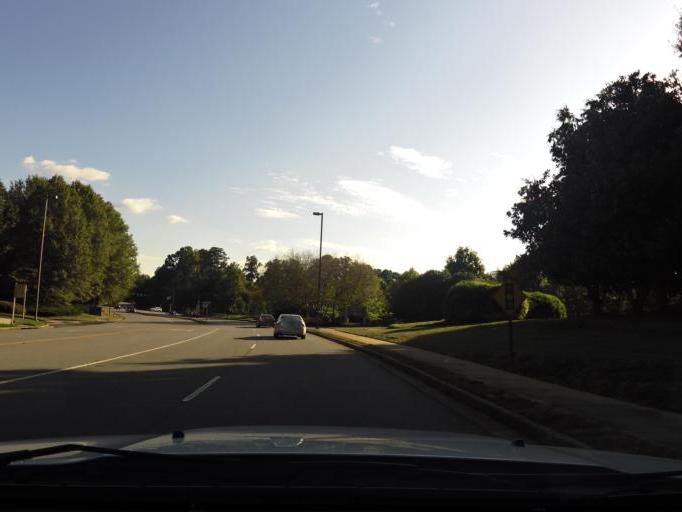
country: US
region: Georgia
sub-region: Cobb County
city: Kennesaw
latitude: 34.0062
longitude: -84.5863
